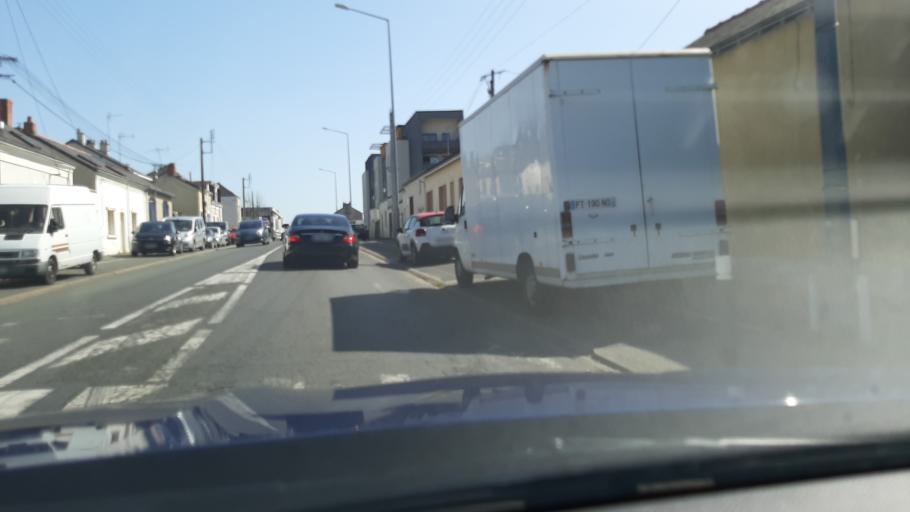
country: FR
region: Pays de la Loire
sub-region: Departement de Maine-et-Loire
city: Les Ponts-de-Ce
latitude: 47.4482
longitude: -0.5114
